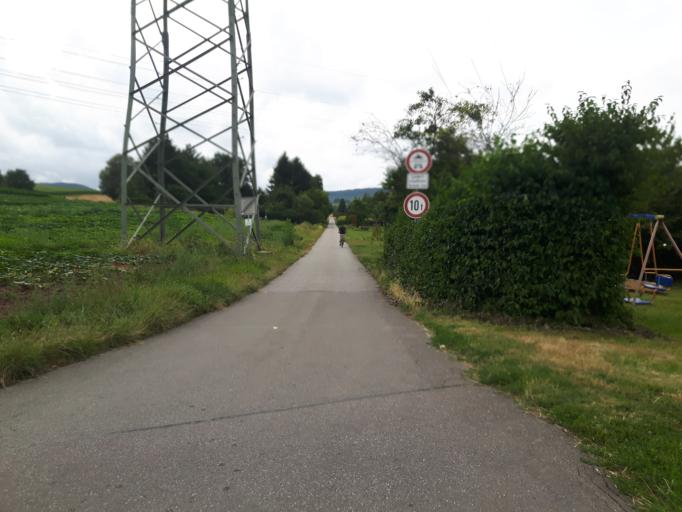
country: DE
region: Baden-Wuerttemberg
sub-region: Regierungsbezirk Stuttgart
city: Nordheim
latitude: 49.1099
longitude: 9.1206
